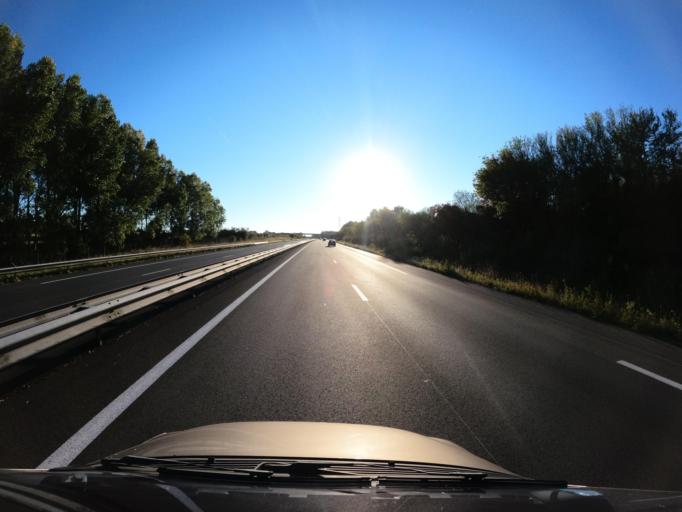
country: FR
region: Pays de la Loire
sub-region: Departement de la Vendee
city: Vendrennes
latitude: 46.8686
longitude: -1.1278
